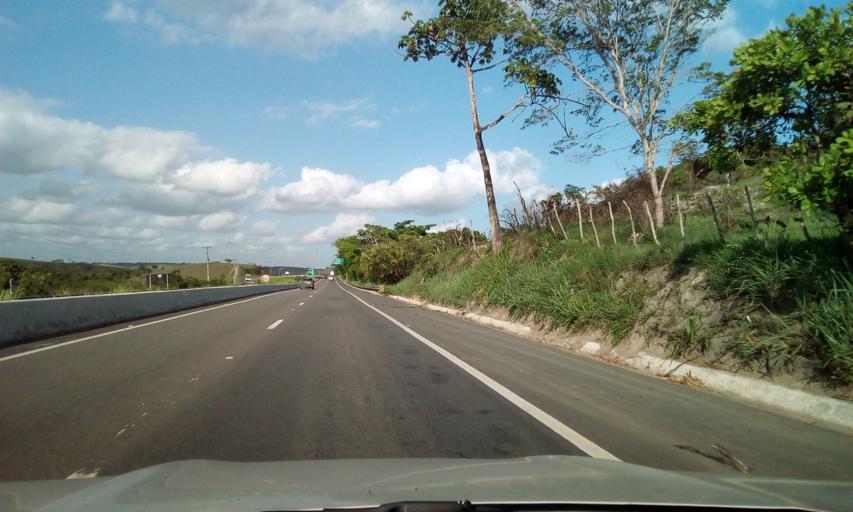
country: BR
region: Pernambuco
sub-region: Ribeirao
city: Ribeirao
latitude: -8.4565
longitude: -35.3607
